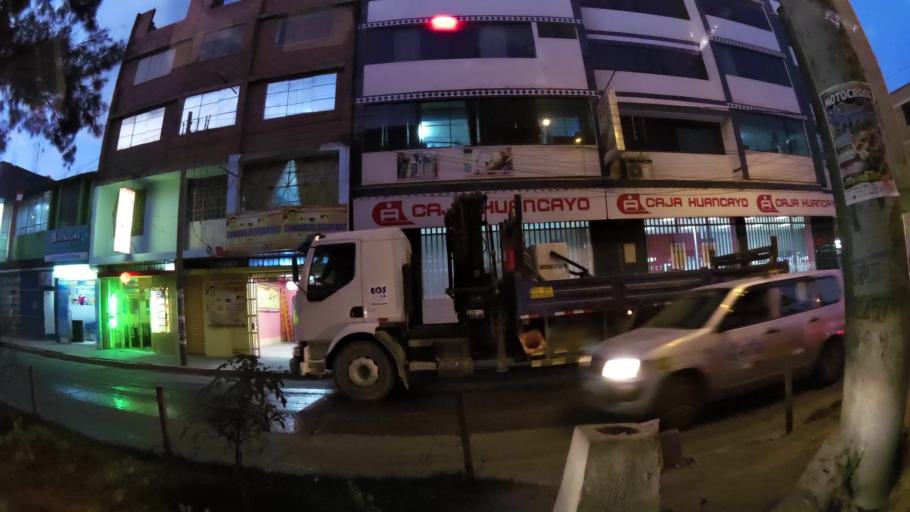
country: PE
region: Junin
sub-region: Provincia de Huancayo
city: El Tambo
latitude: -12.0651
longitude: -75.2179
